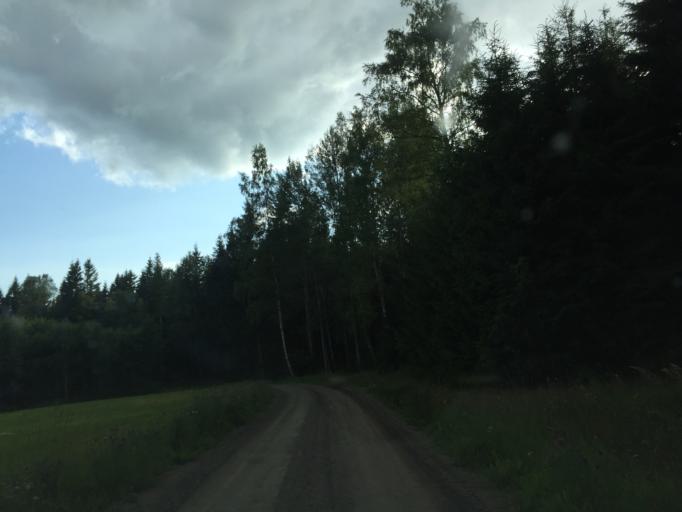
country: SE
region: OEstergoetland
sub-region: Motala Kommun
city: Ryd
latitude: 58.7038
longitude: 15.0471
